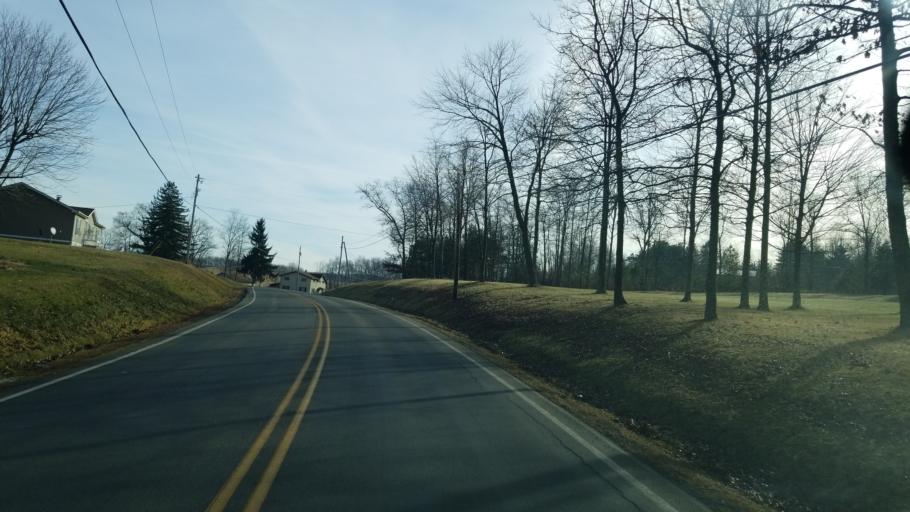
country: US
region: Pennsylvania
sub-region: Indiana County
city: Chevy Chase Heights
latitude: 40.7488
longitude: -79.1117
